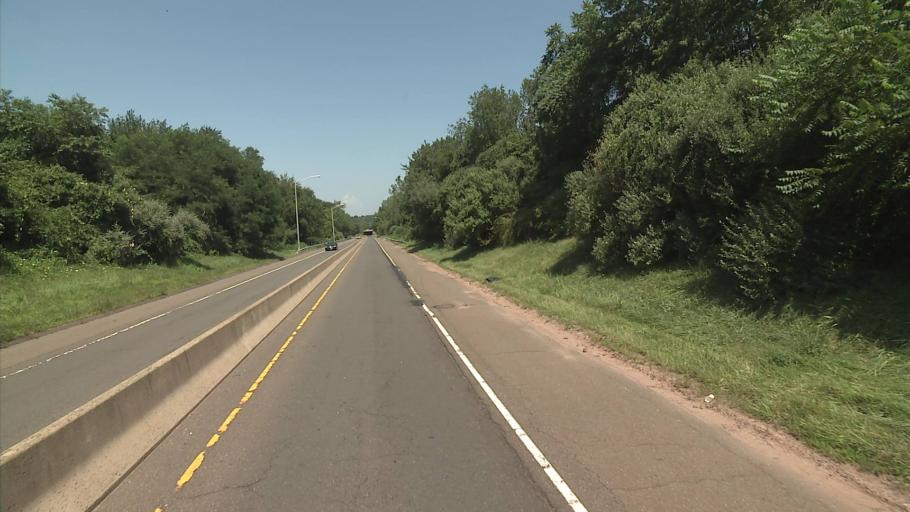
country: US
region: Connecticut
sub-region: New Haven County
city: Branford
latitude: 41.2807
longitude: -72.8346
